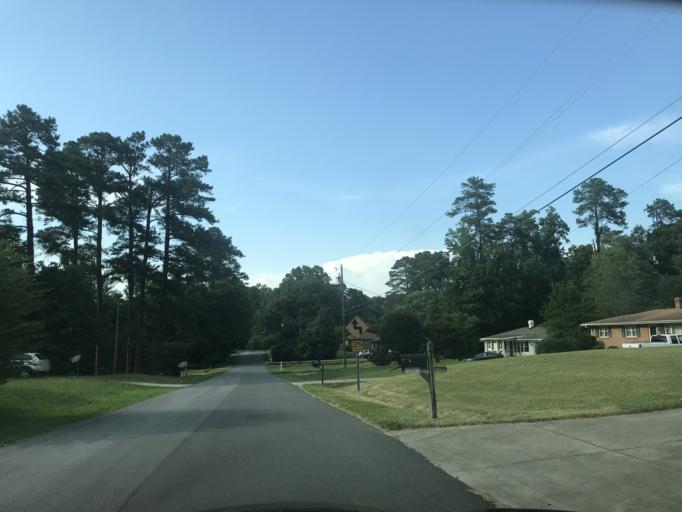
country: US
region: North Carolina
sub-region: Wake County
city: Raleigh
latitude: 35.8170
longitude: -78.5715
